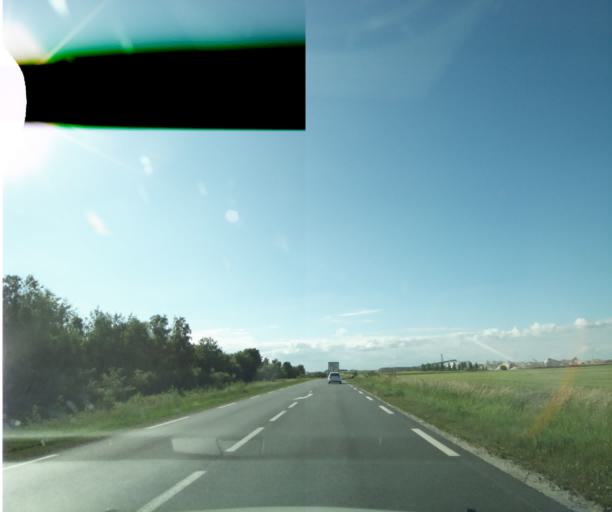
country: FR
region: Centre
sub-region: Departement d'Eure-et-Loir
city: Voves
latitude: 48.2806
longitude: 1.7317
